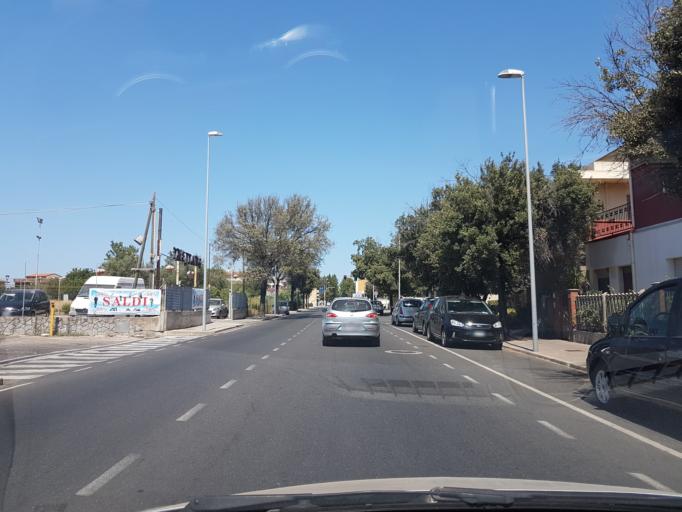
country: IT
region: Sardinia
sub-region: Provincia di Oristano
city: Oristano
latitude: 39.8945
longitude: 8.5969
